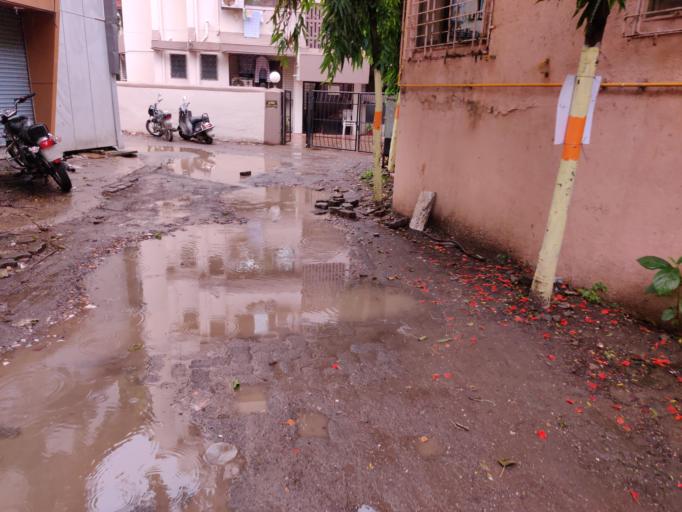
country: IN
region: Maharashtra
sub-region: Mumbai Suburban
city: Borivli
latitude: 19.2578
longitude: 72.8597
